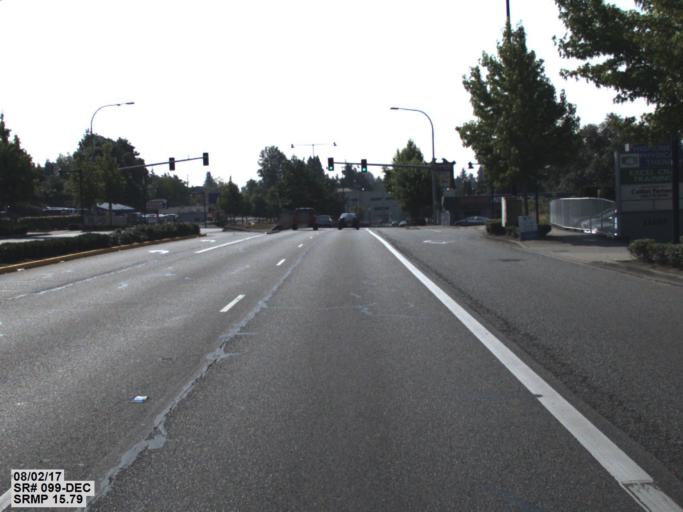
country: US
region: Washington
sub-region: King County
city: Des Moines
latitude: 47.3979
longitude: -122.2960
